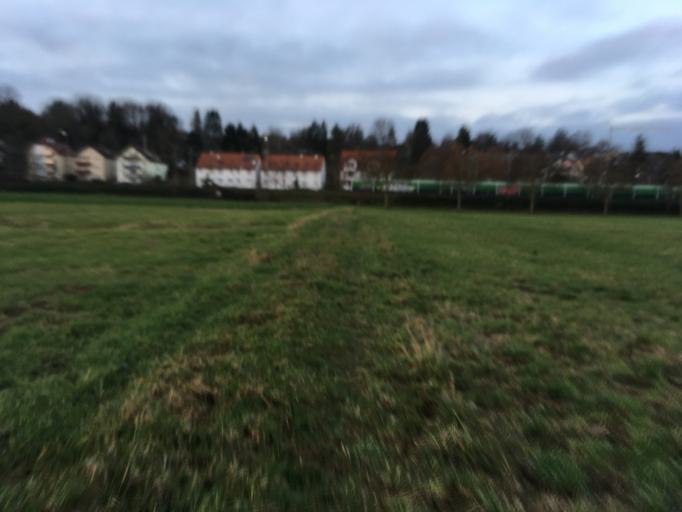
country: DE
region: Baden-Wuerttemberg
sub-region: Regierungsbezirk Stuttgart
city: Flein
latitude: 49.1243
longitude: 9.1836
